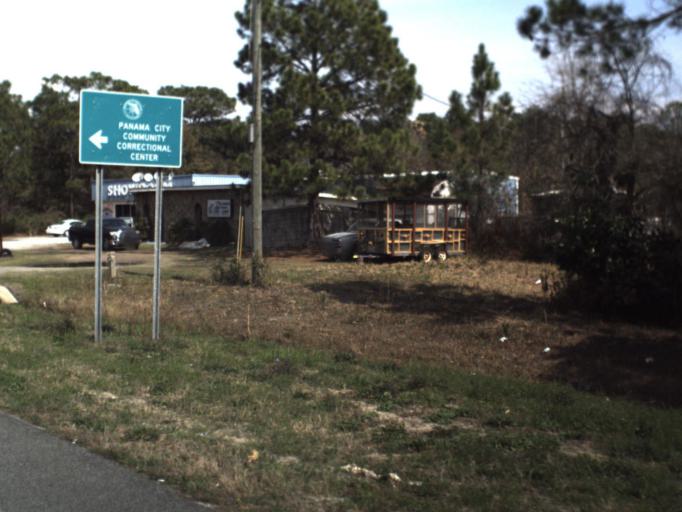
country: US
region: Florida
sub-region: Bay County
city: Pretty Bayou
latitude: 30.2125
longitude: -85.6714
